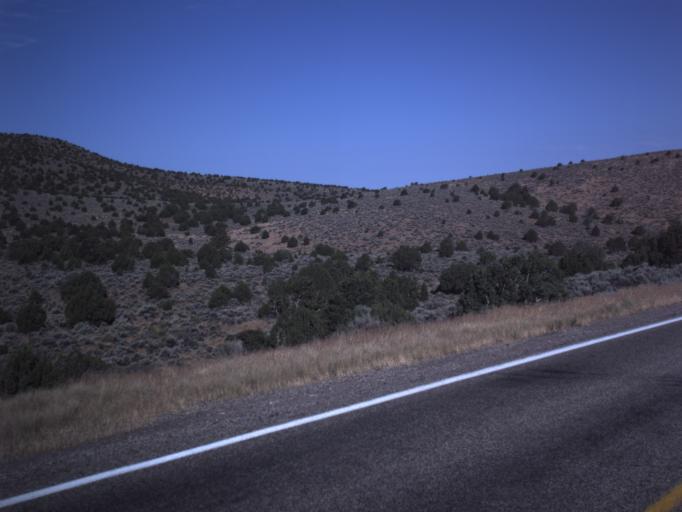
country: US
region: Utah
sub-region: Beaver County
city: Milford
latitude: 38.1248
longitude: -112.9546
